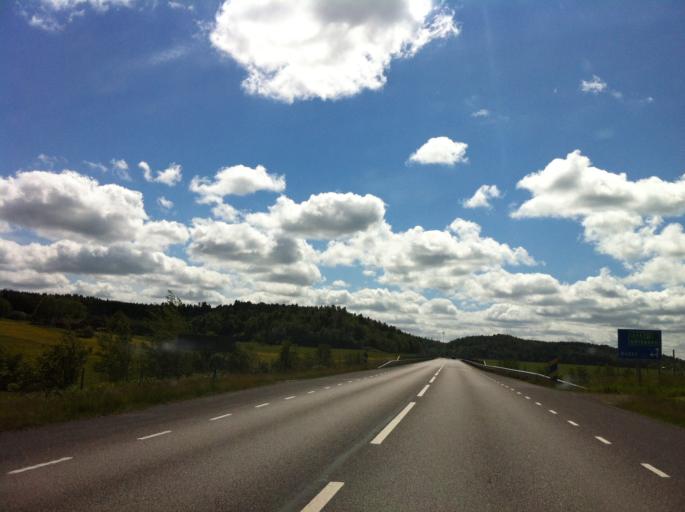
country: SE
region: Vaestra Goetaland
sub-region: Trollhattan
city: Sjuntorp
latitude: 58.2020
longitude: 12.1562
